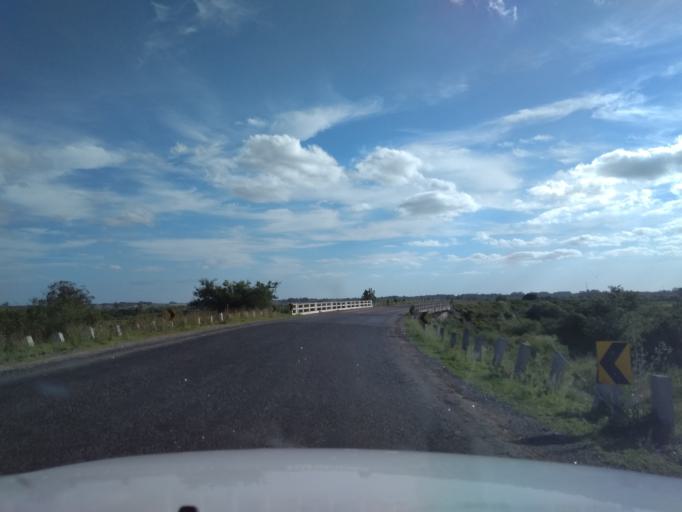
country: UY
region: Canelones
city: San Ramon
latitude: -34.2655
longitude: -55.9285
